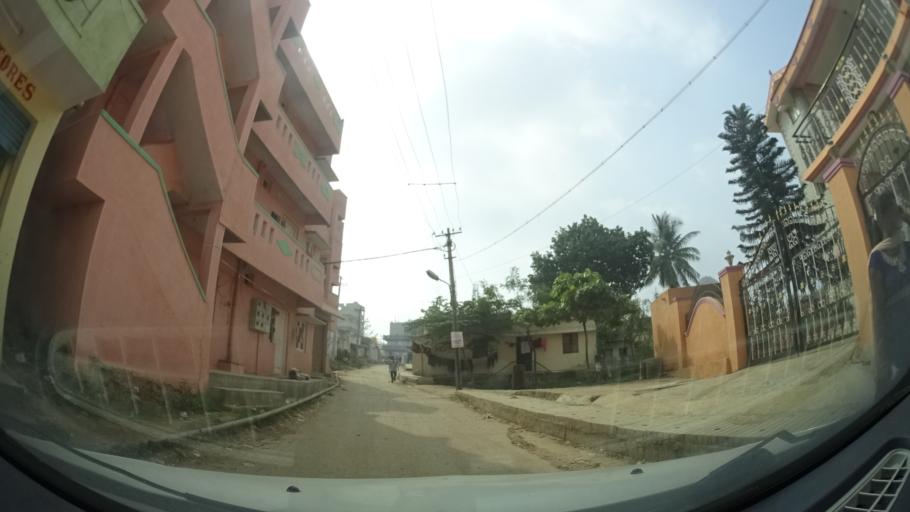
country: IN
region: Karnataka
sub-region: Bangalore Urban
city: Anekal
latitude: 12.8244
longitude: 77.6688
